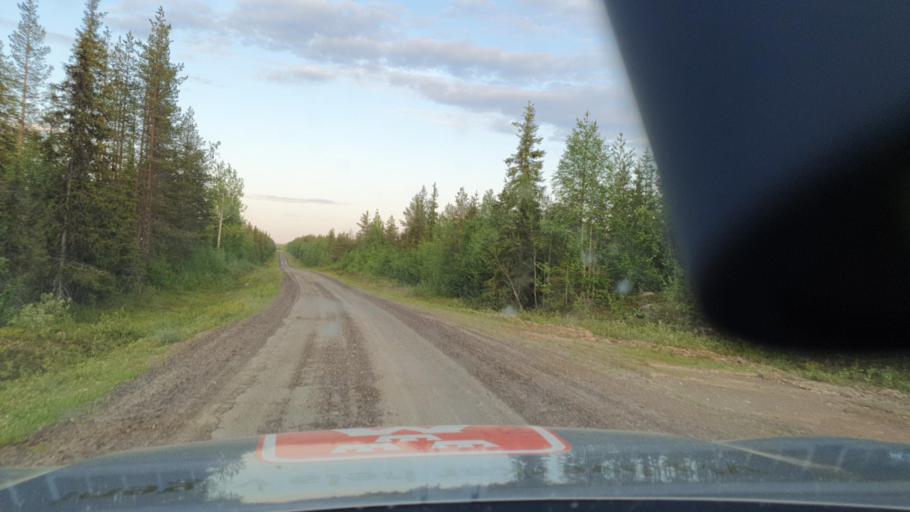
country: SE
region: Norrbotten
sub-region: Bodens Kommun
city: Boden
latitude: 66.4951
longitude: 21.5625
